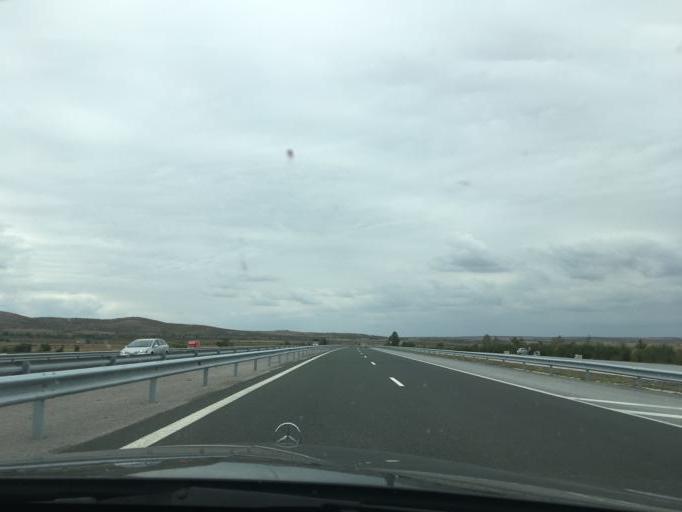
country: BG
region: Sliven
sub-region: Obshtina Sliven
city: Kermen
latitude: 42.5034
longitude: 26.3056
